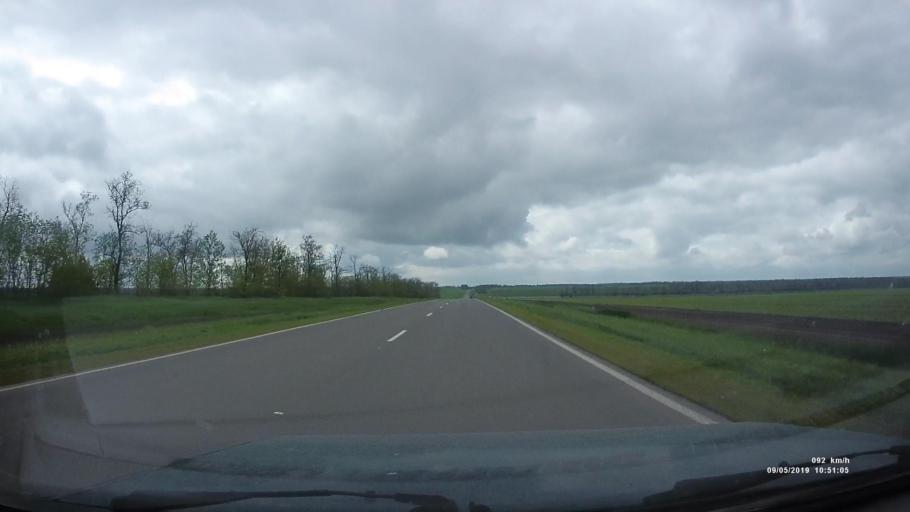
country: RU
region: Rostov
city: Peshkovo
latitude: 46.9197
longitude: 39.3553
